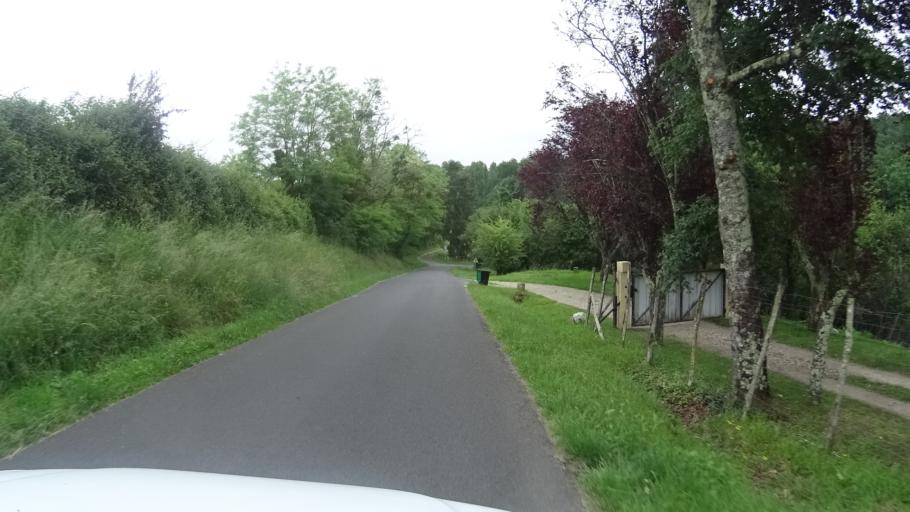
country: FR
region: Aquitaine
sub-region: Departement de la Dordogne
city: Bergerac
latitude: 44.8783
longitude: 0.4790
